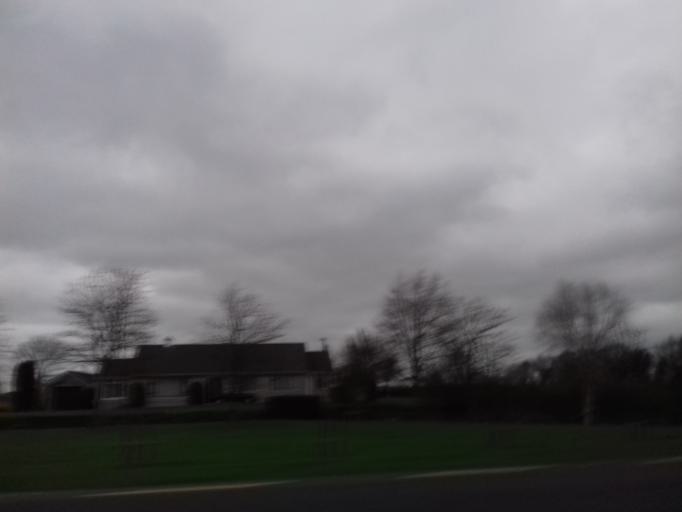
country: IE
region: Munster
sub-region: County Limerick
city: Adare
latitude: 52.5436
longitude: -8.8515
